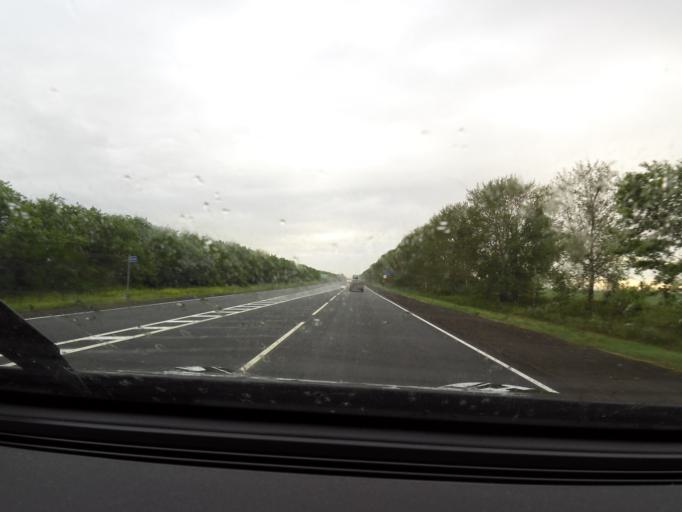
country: RU
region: Chuvashia
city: Yantikovo
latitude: 55.8030
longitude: 47.8987
